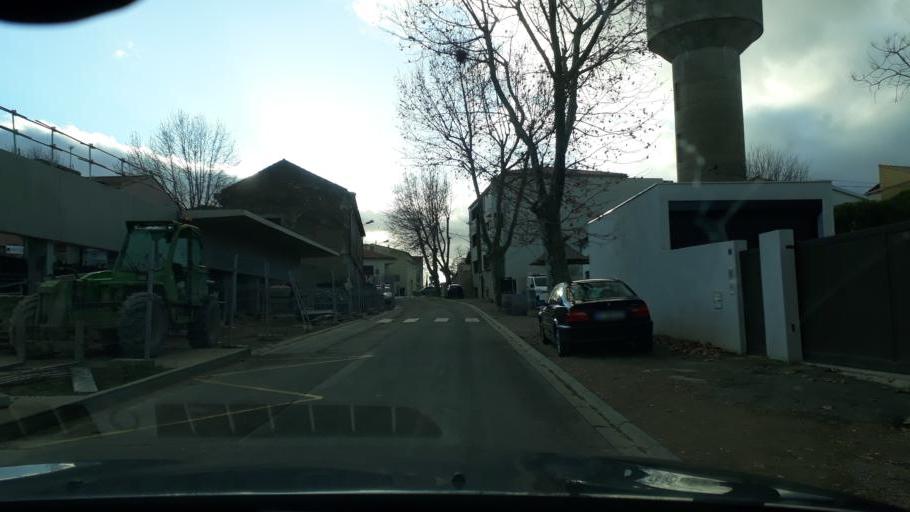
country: FR
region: Languedoc-Roussillon
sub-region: Departement de l'Herault
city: Colombiers
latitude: 43.3132
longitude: 3.1420
